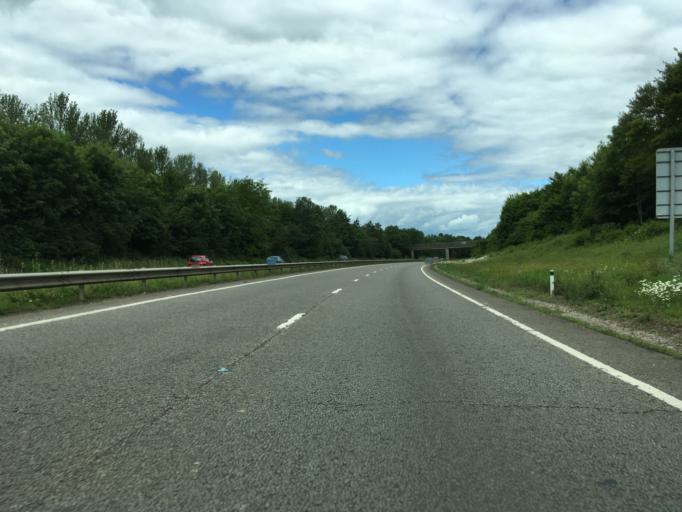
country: GB
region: England
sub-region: Milton Keynes
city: Milton Keynes
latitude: 52.0157
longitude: -0.7554
